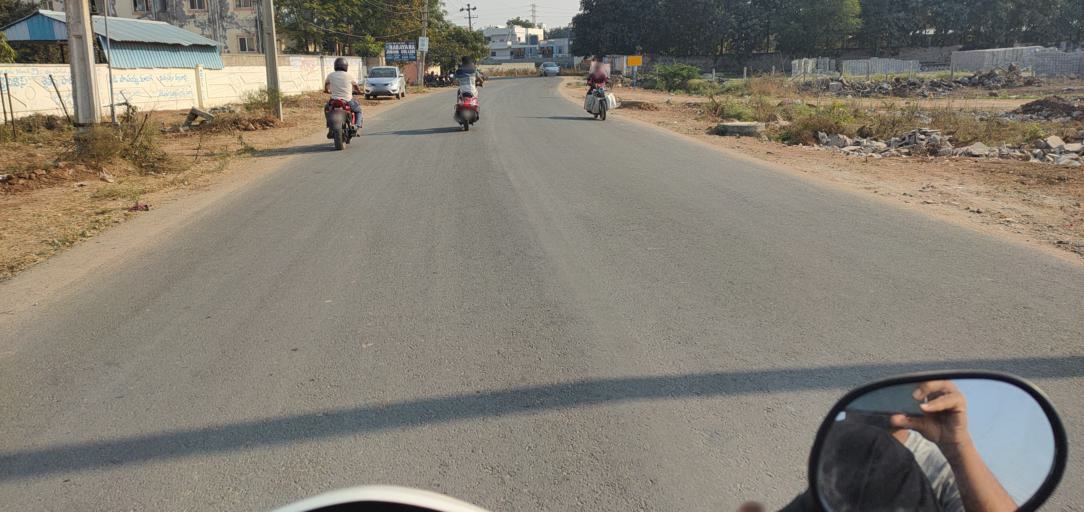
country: IN
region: Telangana
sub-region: Rangareddi
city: Lal Bahadur Nagar
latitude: 17.3412
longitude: 78.6226
